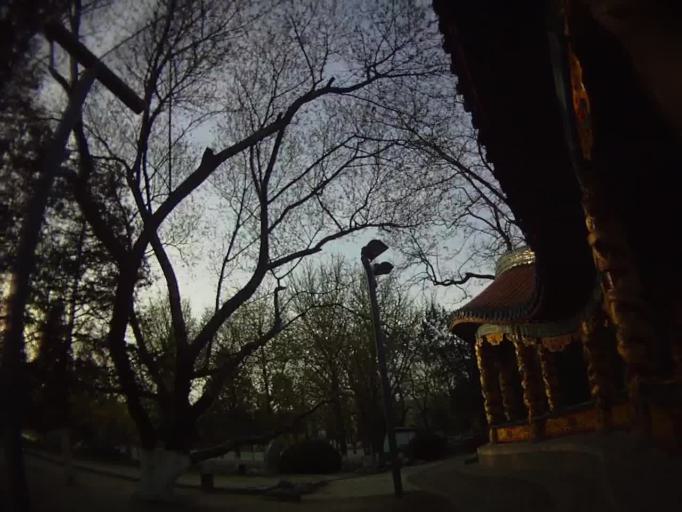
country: CN
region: Beijing
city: Longtan
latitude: 39.8787
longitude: 116.4319
